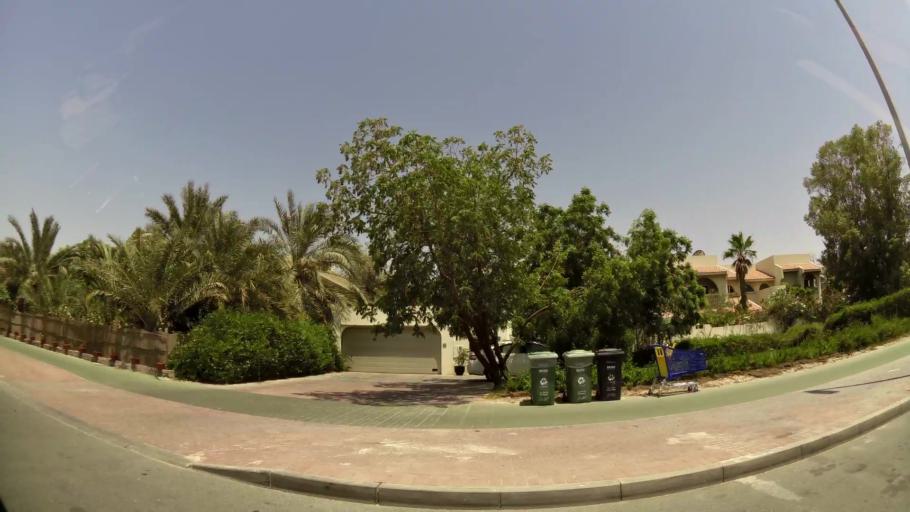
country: AE
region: Dubai
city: Dubai
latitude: 25.1842
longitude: 55.2340
